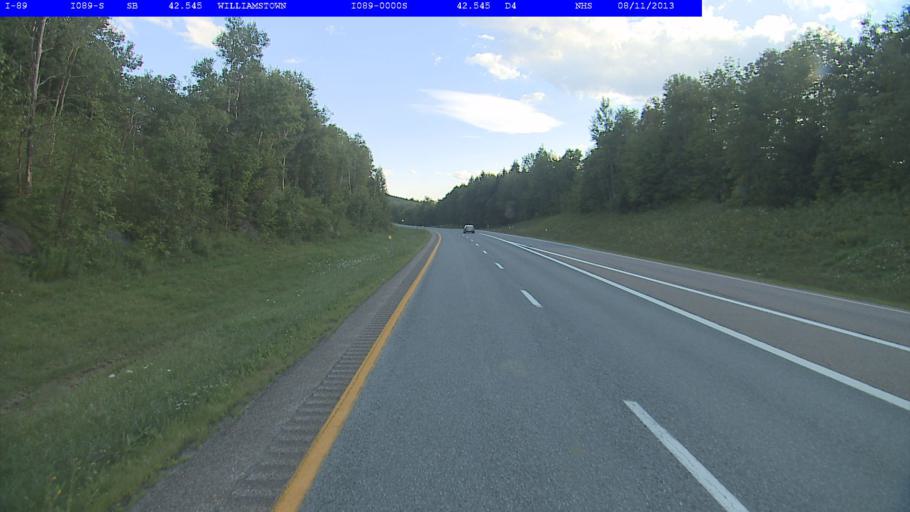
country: US
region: Vermont
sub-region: Washington County
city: Northfield
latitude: 44.1098
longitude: -72.6115
